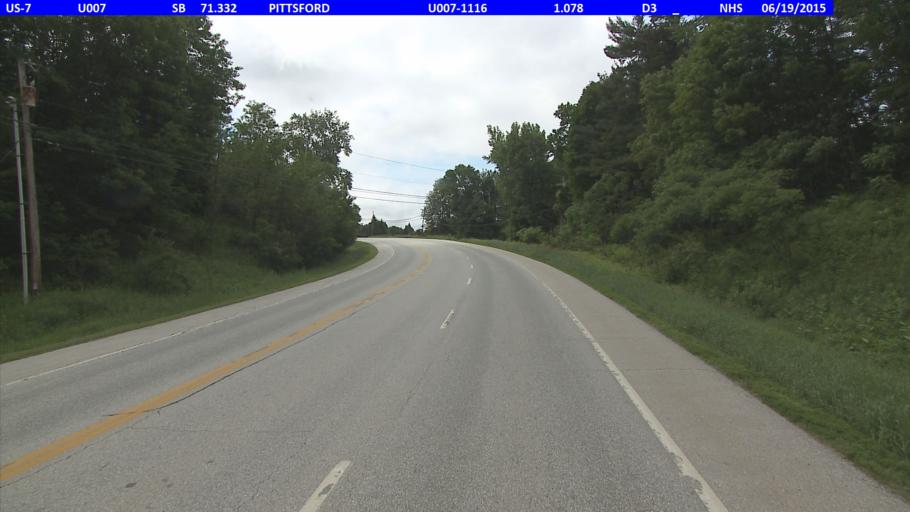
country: US
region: Vermont
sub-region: Rutland County
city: Rutland
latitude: 43.6815
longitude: -72.9930
